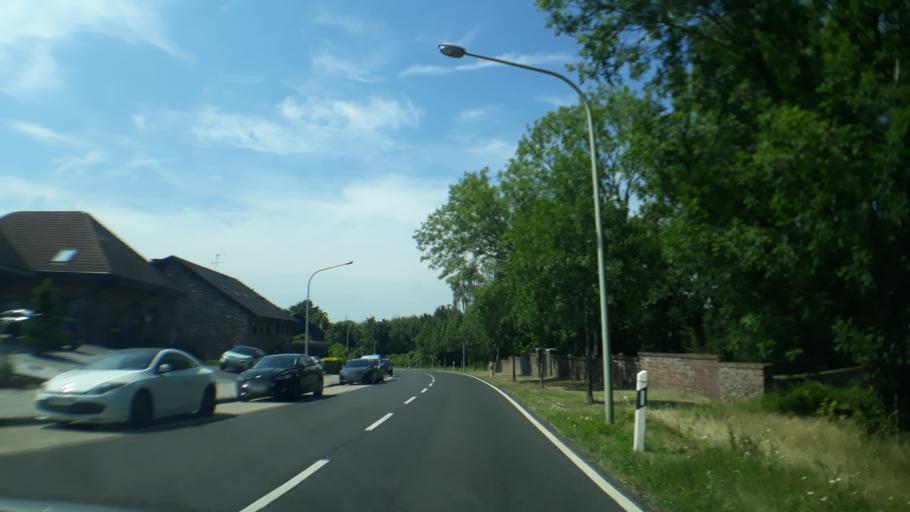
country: DE
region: North Rhine-Westphalia
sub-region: Regierungsbezirk Koln
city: Langerwehe
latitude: 50.8253
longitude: 6.3279
